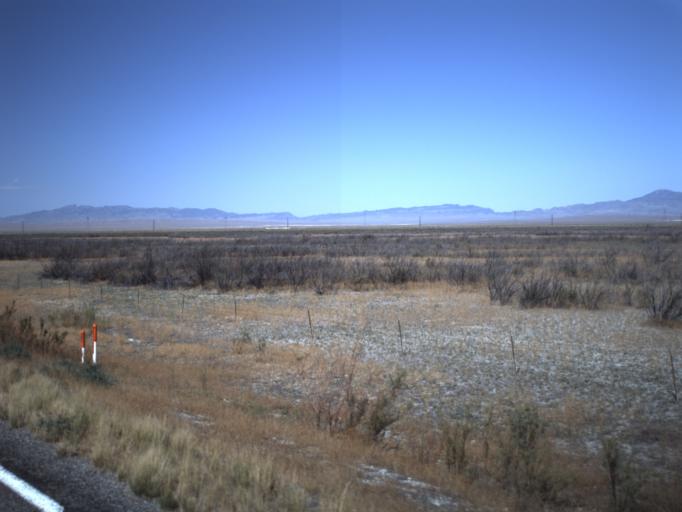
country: US
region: Utah
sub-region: Millard County
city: Delta
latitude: 39.2635
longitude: -112.8748
